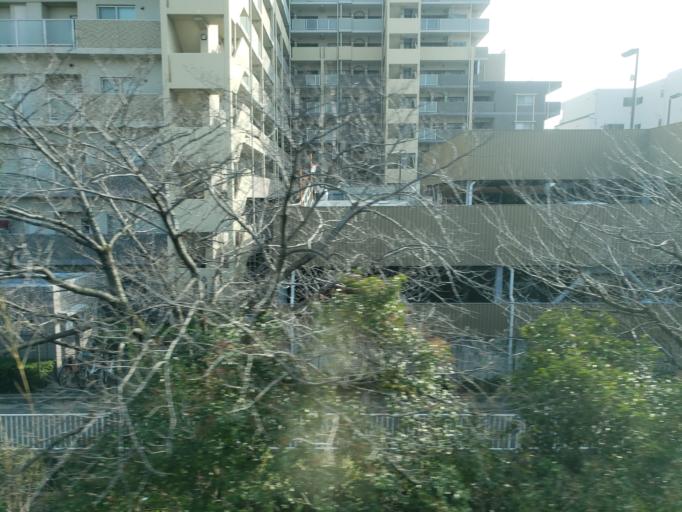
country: JP
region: Hyogo
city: Amagasaki
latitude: 34.7389
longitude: 135.3892
